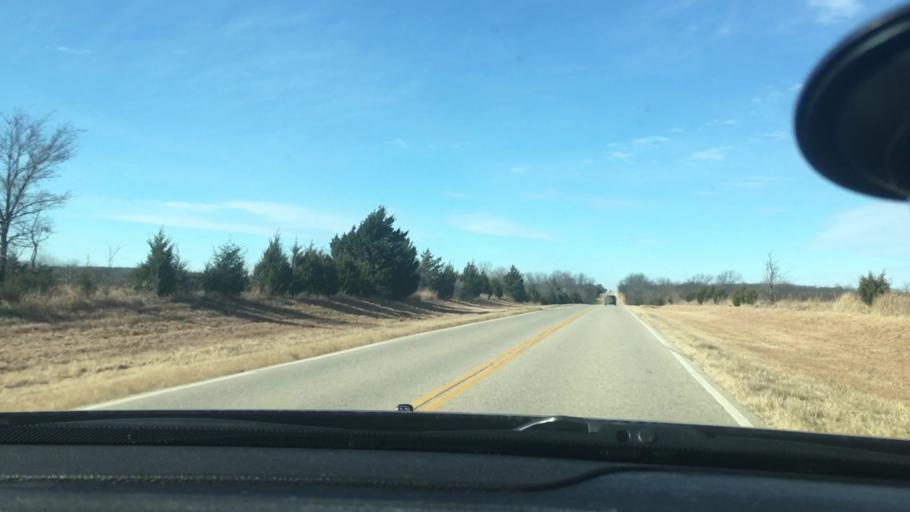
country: US
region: Oklahoma
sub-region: Garvin County
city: Stratford
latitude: 34.9859
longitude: -97.0019
